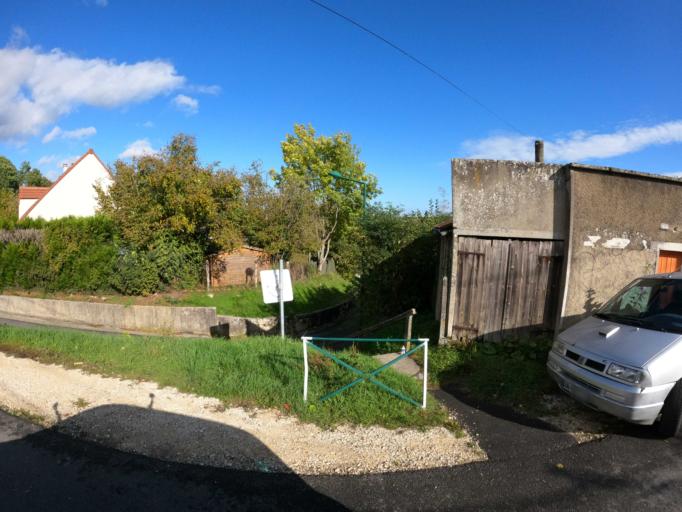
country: FR
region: Ile-de-France
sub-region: Departement de Seine-et-Marne
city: Montry
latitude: 48.8869
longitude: 2.8238
